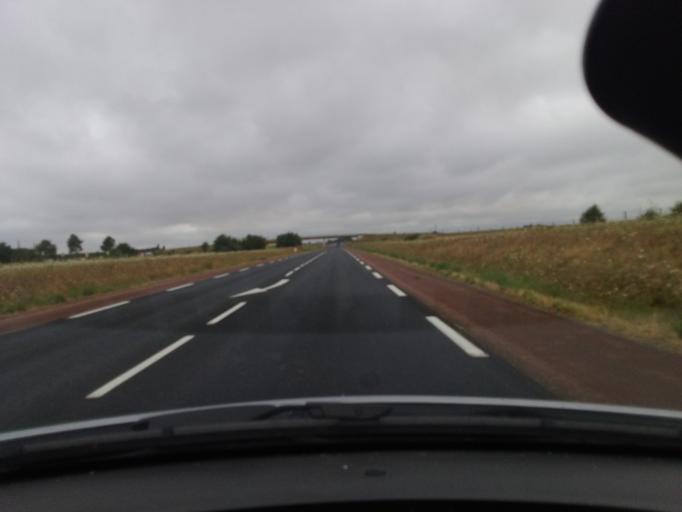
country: FR
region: Pays de la Loire
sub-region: Departement de la Vendee
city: Lucon
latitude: 46.4714
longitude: -1.1626
